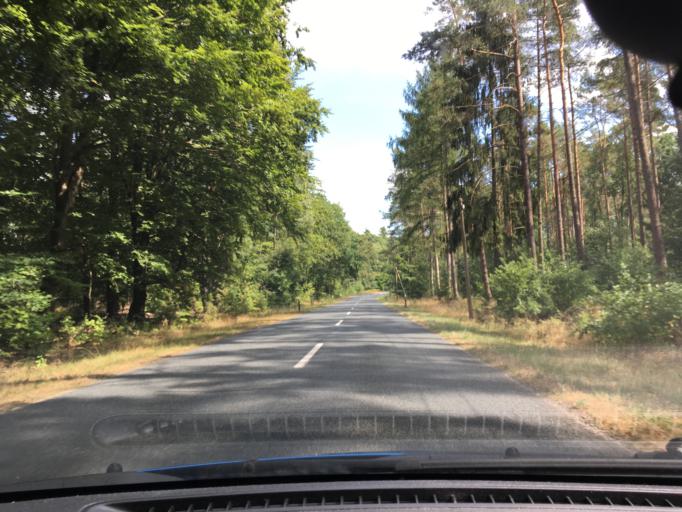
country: DE
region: Lower Saxony
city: Rehlingen
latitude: 53.0806
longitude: 10.2237
